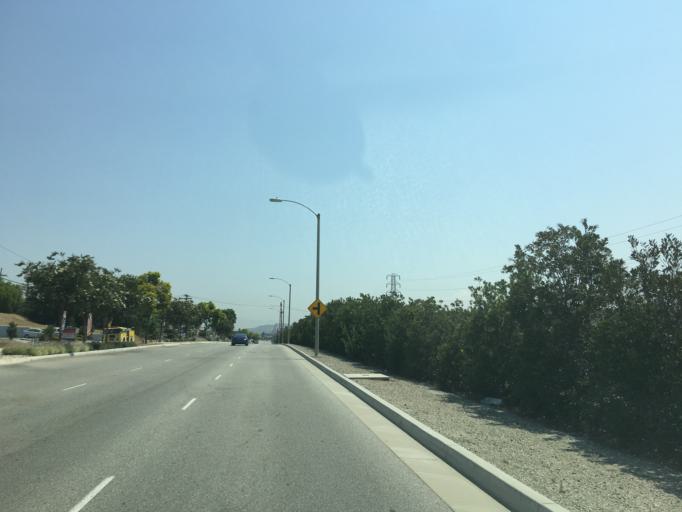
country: US
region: California
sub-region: Los Angeles County
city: Walnut
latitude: 34.0061
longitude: -117.8653
